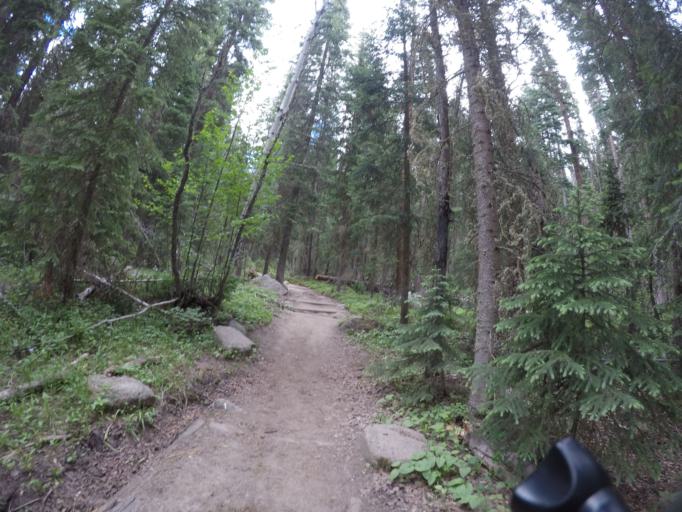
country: US
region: Colorado
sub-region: Grand County
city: Granby
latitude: 40.3085
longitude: -105.8376
